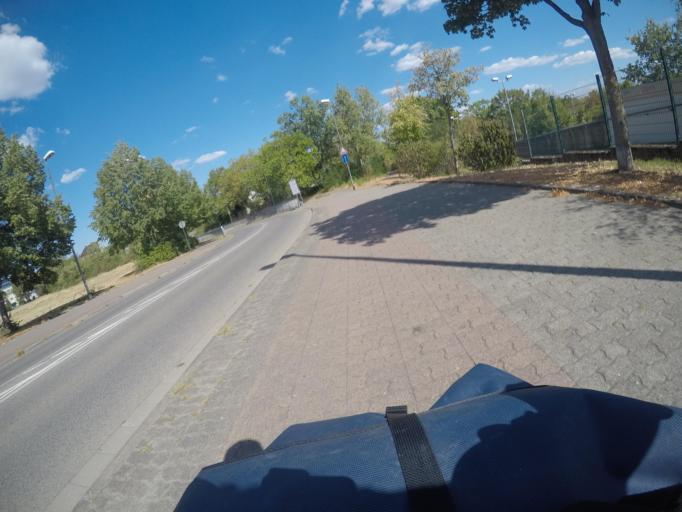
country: DE
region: Rheinland-Pfalz
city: Gartenstadt
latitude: 49.4839
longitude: 8.4139
